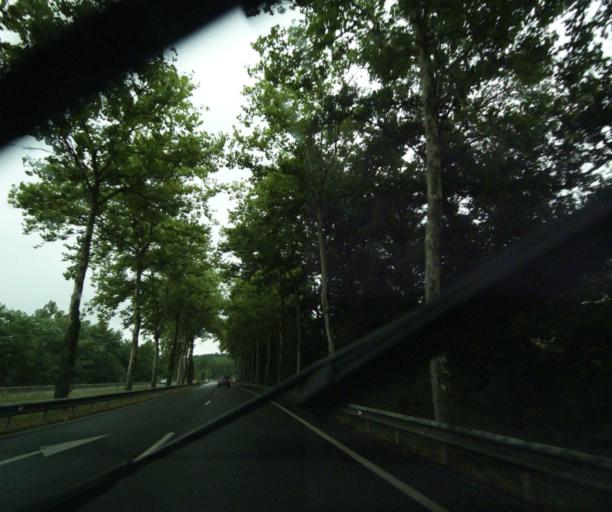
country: FR
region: Midi-Pyrenees
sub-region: Departement du Tarn
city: Le Garric
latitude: 43.9875
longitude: 2.1743
